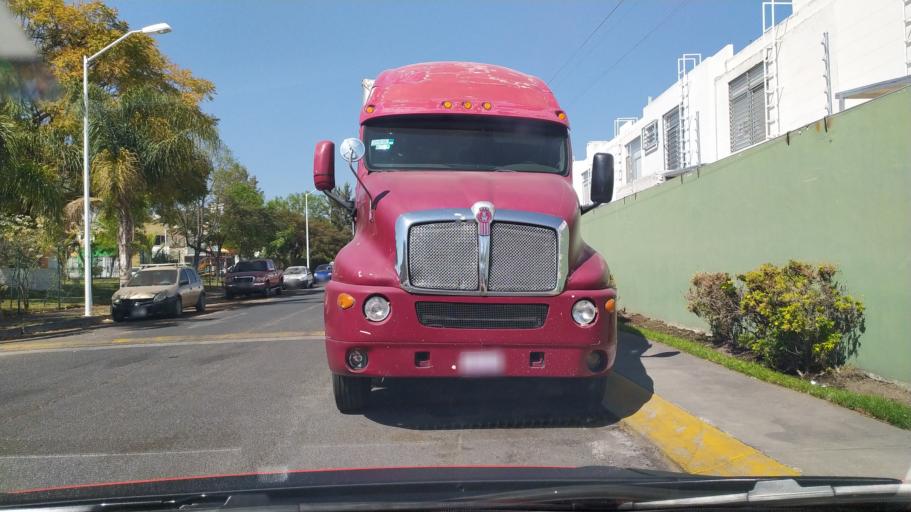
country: MX
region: Jalisco
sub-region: Tlajomulco de Zuniga
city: Palomar
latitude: 20.6292
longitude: -103.4633
